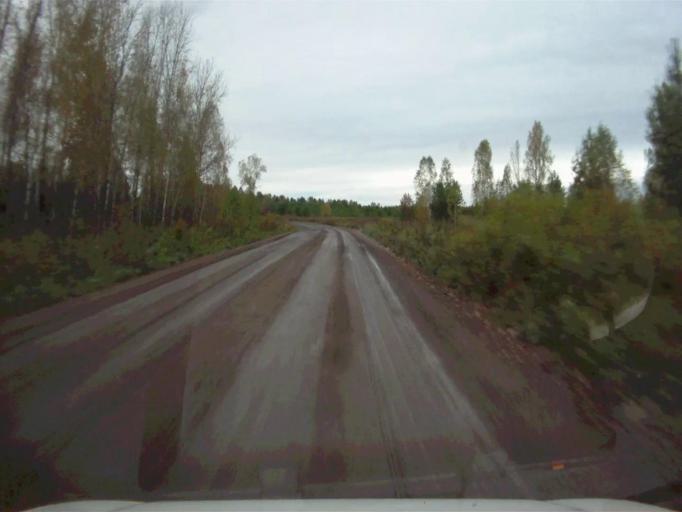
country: RU
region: Chelyabinsk
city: Nyazepetrovsk
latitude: 56.1376
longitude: 59.3002
